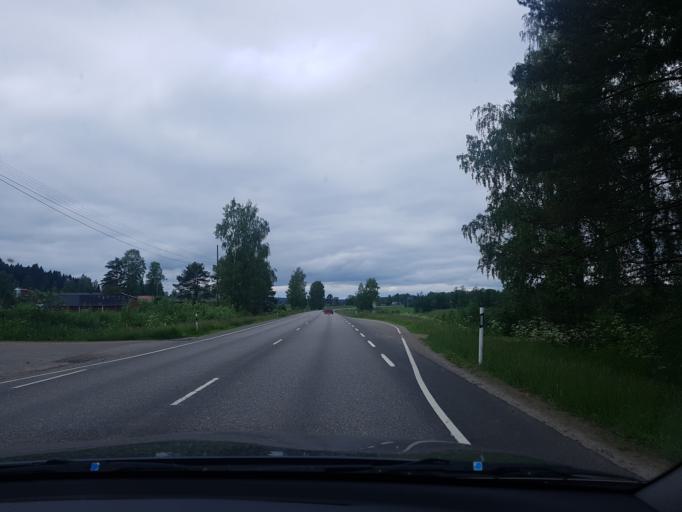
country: FI
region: Pirkanmaa
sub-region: Tampere
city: Paelkaene
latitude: 61.2513
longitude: 24.3531
